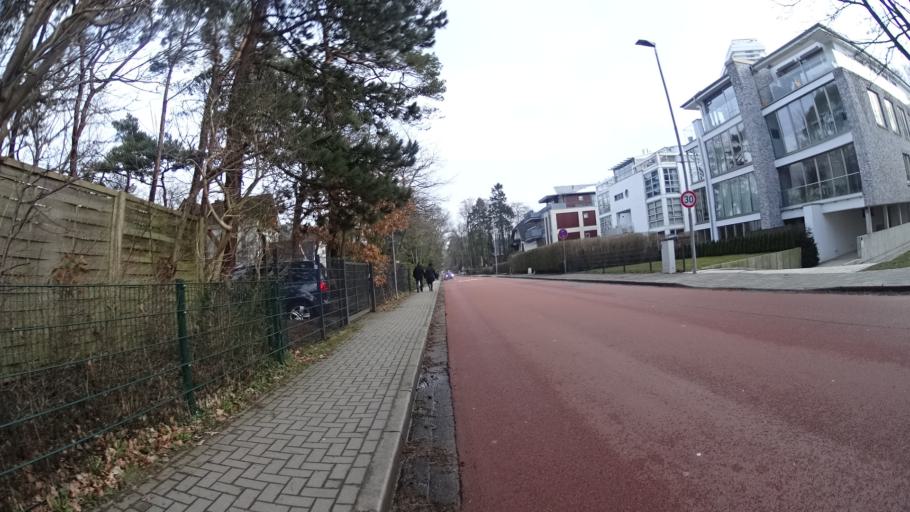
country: DE
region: Schleswig-Holstein
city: Timmendorfer Strand
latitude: 54.0081
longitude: 10.7718
